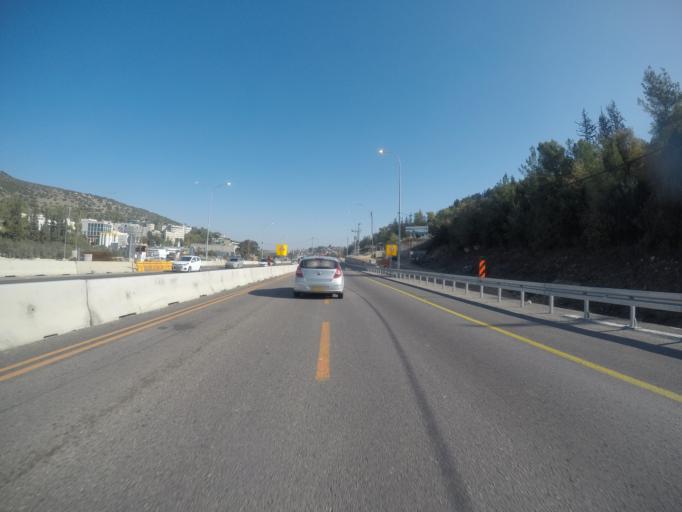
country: IL
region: Haifa
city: Daliyat el Karmil
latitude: 32.6542
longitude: 35.0962
